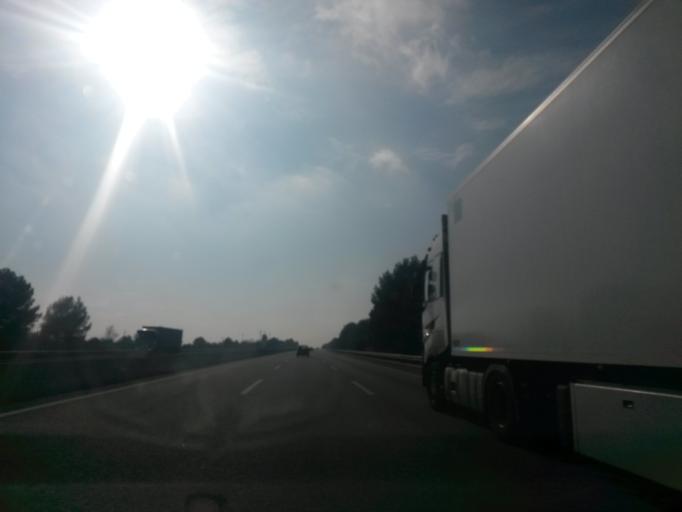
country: ES
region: Catalonia
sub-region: Provincia de Girona
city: Borrassa
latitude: 42.2072
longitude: 2.9382
